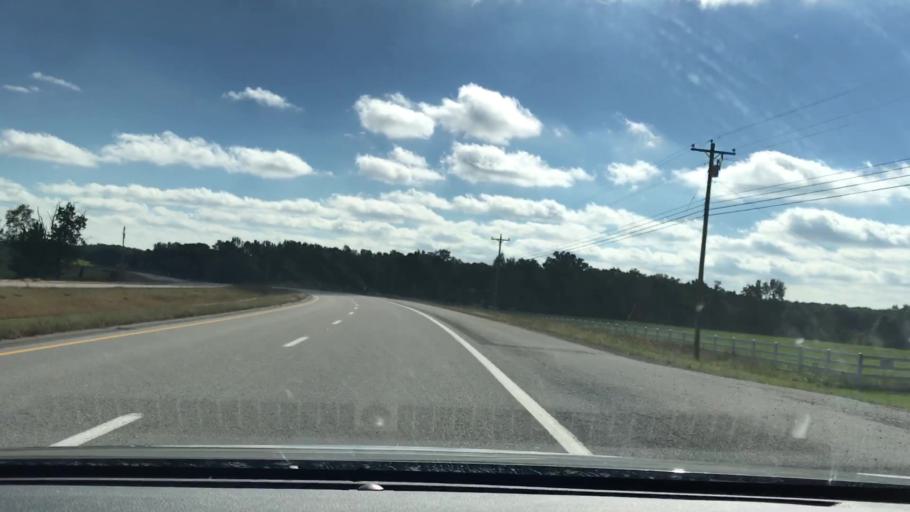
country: US
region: Tennessee
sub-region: Fentress County
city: Grimsley
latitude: 36.3112
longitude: -84.9734
